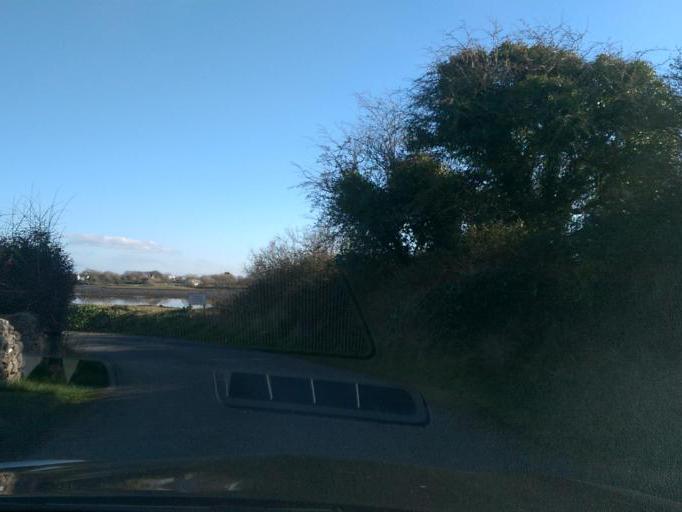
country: IE
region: Connaught
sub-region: County Galway
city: Oranmore
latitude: 53.2397
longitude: -8.9600
